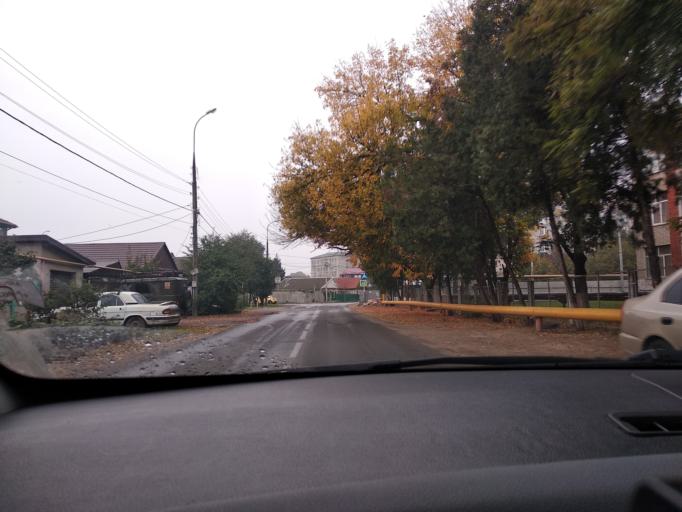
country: RU
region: Krasnodarskiy
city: Krasnodar
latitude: 45.0172
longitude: 38.9970
